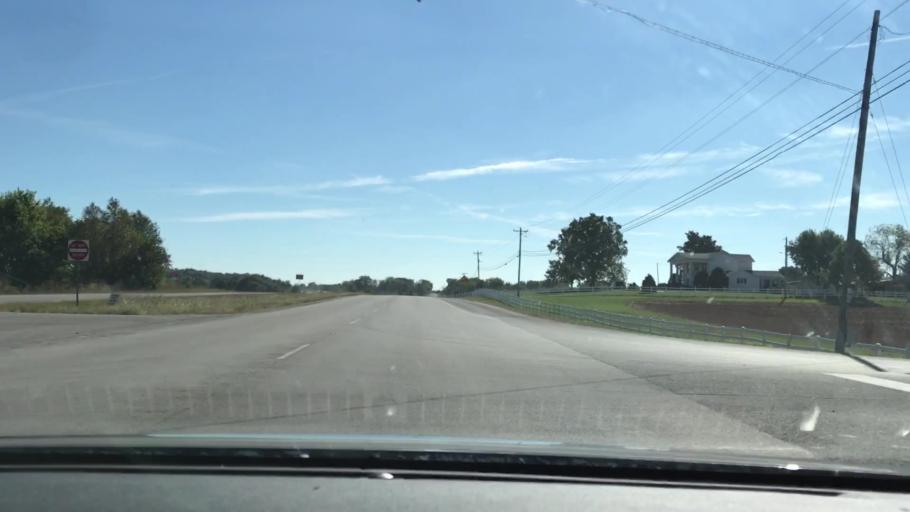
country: US
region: Kentucky
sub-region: Christian County
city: Hopkinsville
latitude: 36.8573
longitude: -87.4245
